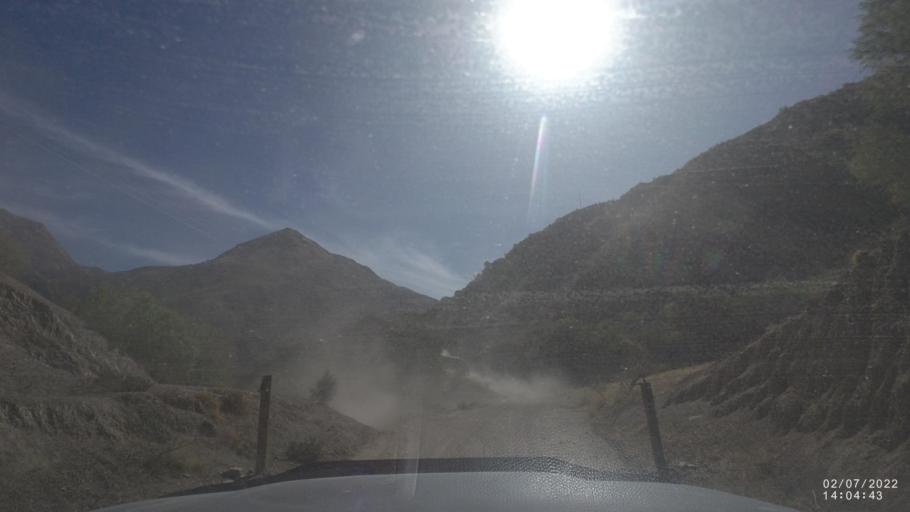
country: BO
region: Cochabamba
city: Irpa Irpa
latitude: -17.8221
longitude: -66.3947
